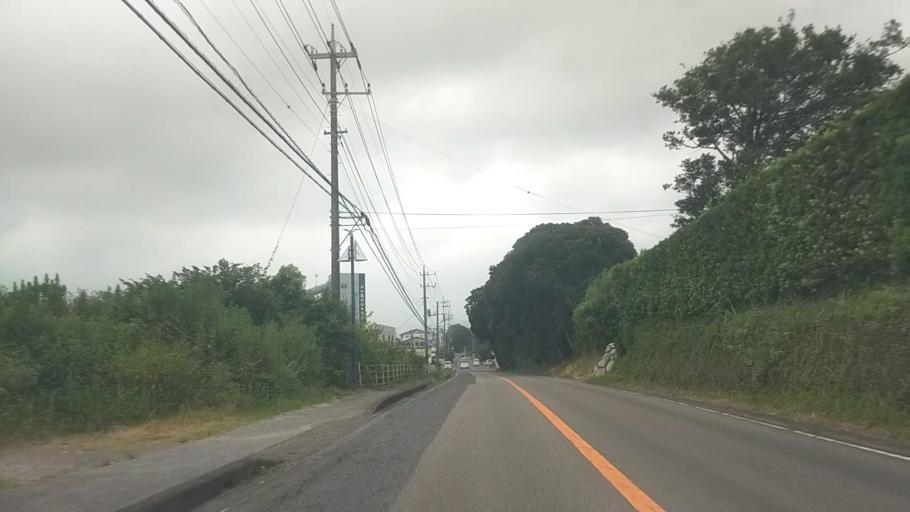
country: JP
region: Chiba
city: Kawaguchi
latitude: 35.1169
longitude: 140.0763
